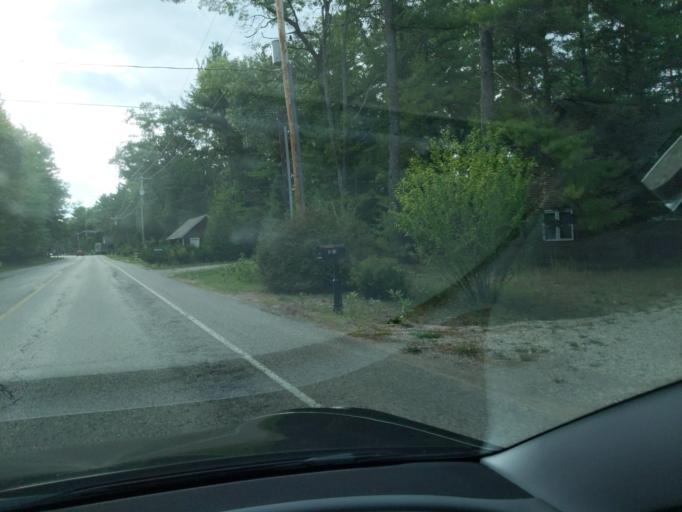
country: US
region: Michigan
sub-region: Kalkaska County
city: Rapid City
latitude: 44.8566
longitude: -85.3002
